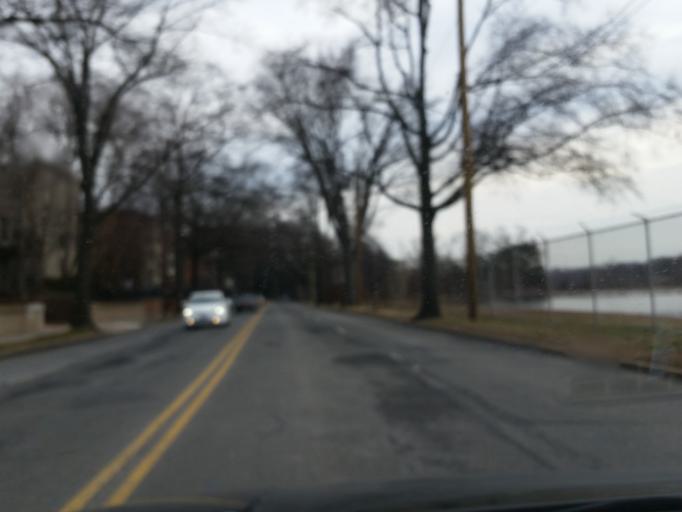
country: US
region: Virginia
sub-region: Arlington County
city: Arlington
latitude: 38.9127
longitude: -77.0911
